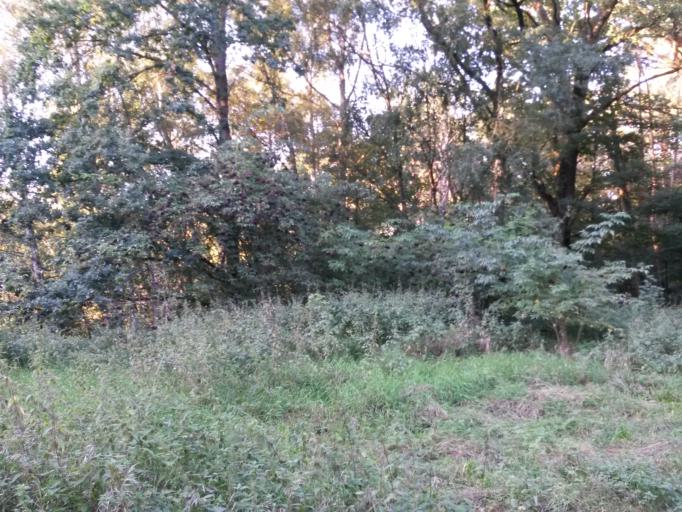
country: DE
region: Brandenburg
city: Templin
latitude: 53.1083
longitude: 13.4732
